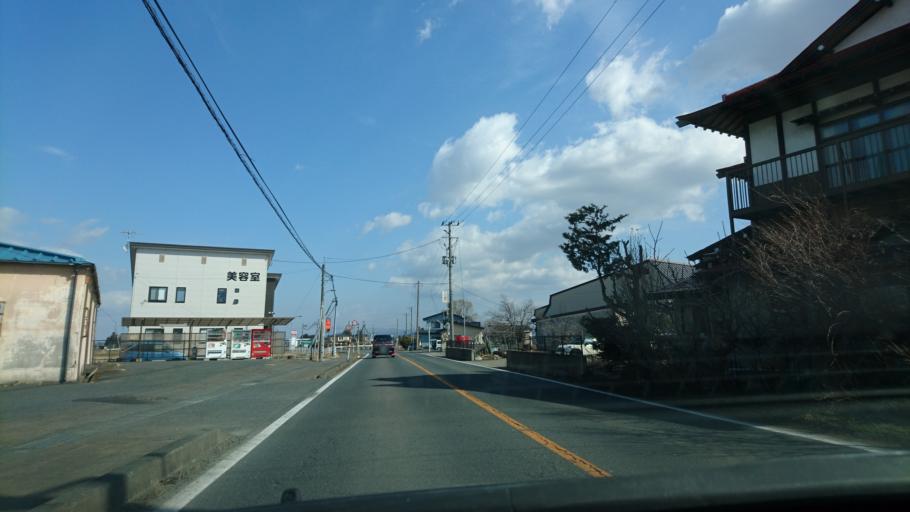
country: JP
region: Iwate
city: Morioka-shi
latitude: 39.5686
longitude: 141.1089
